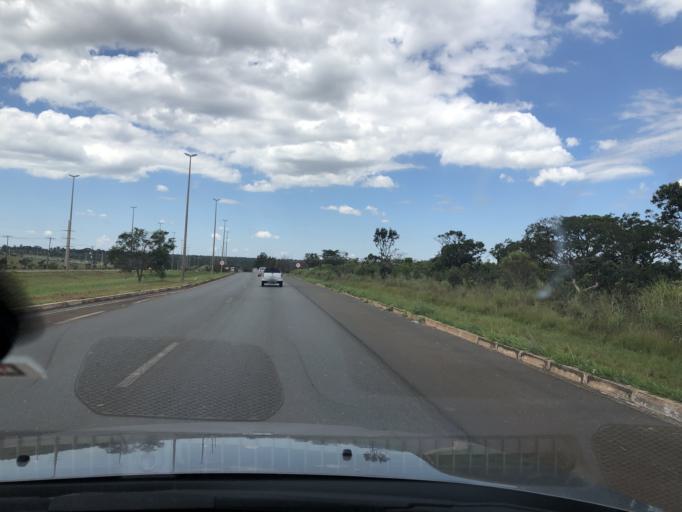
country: BR
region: Federal District
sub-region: Brasilia
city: Brasilia
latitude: -15.9734
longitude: -48.0142
